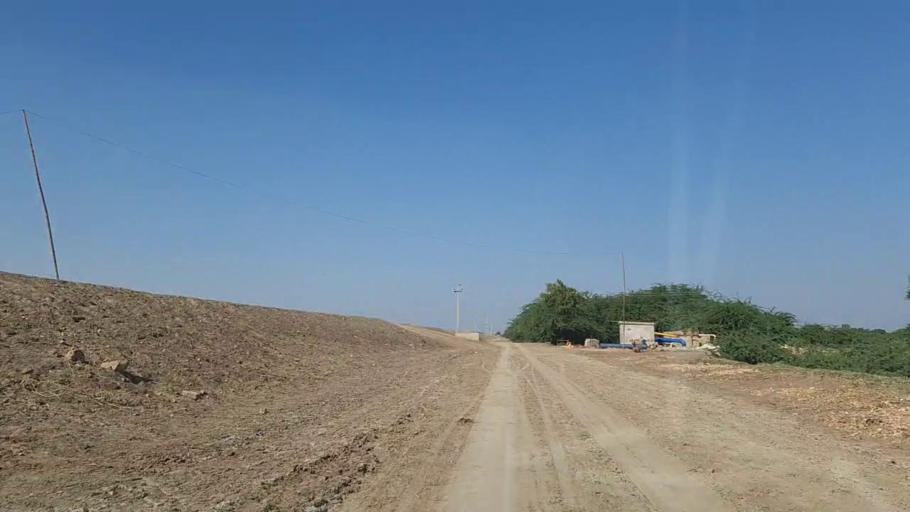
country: PK
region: Sindh
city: Chuhar Jamali
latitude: 24.5377
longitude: 68.0158
